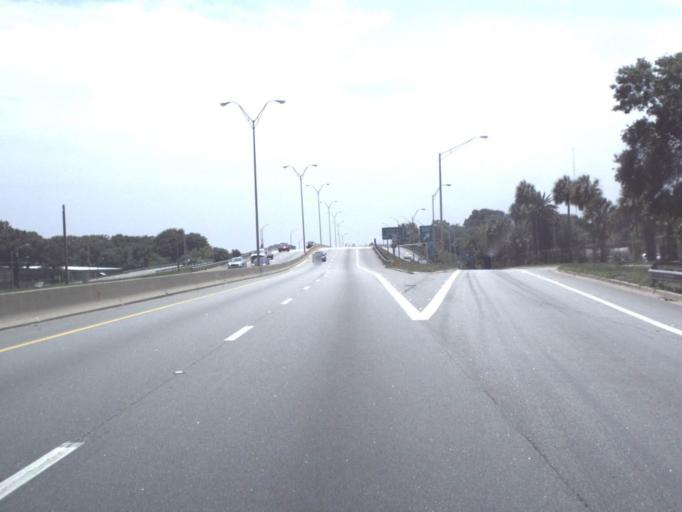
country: US
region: Florida
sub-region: Duval County
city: Jacksonville
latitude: 30.3472
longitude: -81.6369
